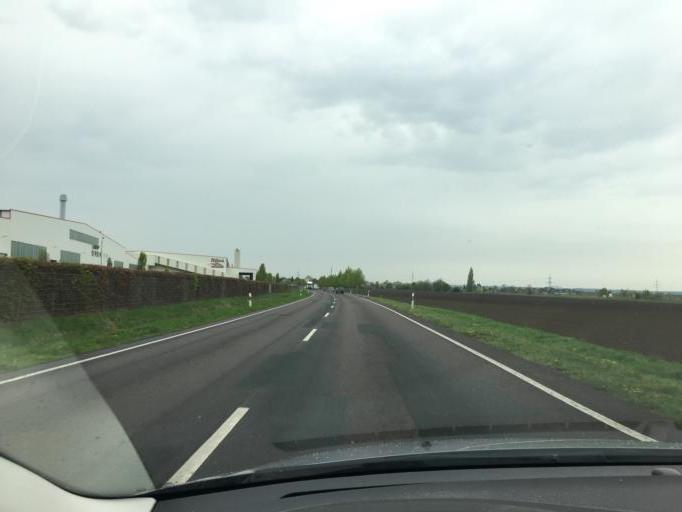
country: DE
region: Saxony-Anhalt
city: Gross Ammensleben
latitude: 52.2253
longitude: 11.5343
